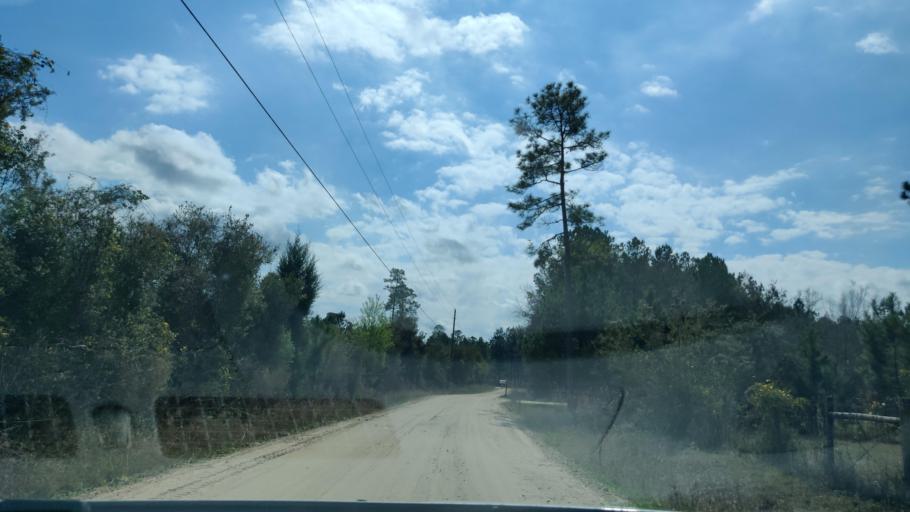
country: US
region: Florida
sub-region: Duval County
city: Baldwin
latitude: 30.1743
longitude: -81.9571
